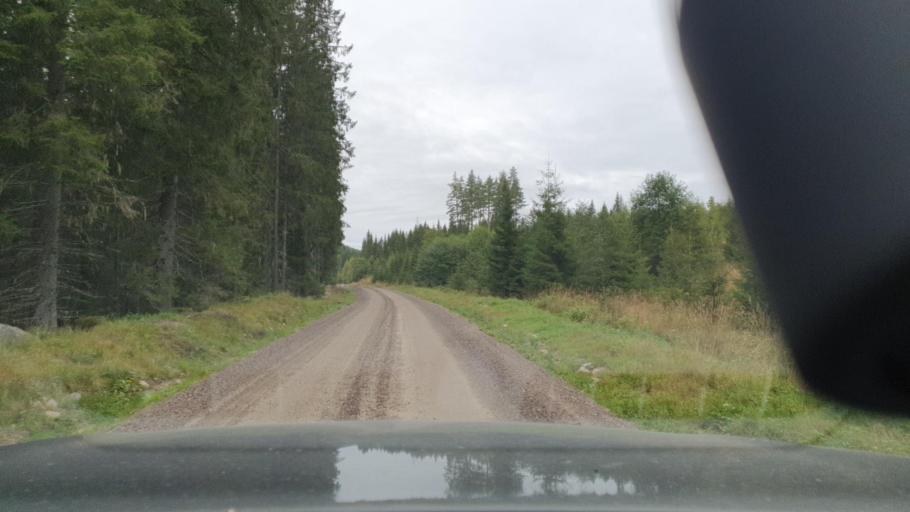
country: SE
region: Vaermland
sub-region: Eda Kommun
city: Charlottenberg
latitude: 60.0368
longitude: 12.5910
